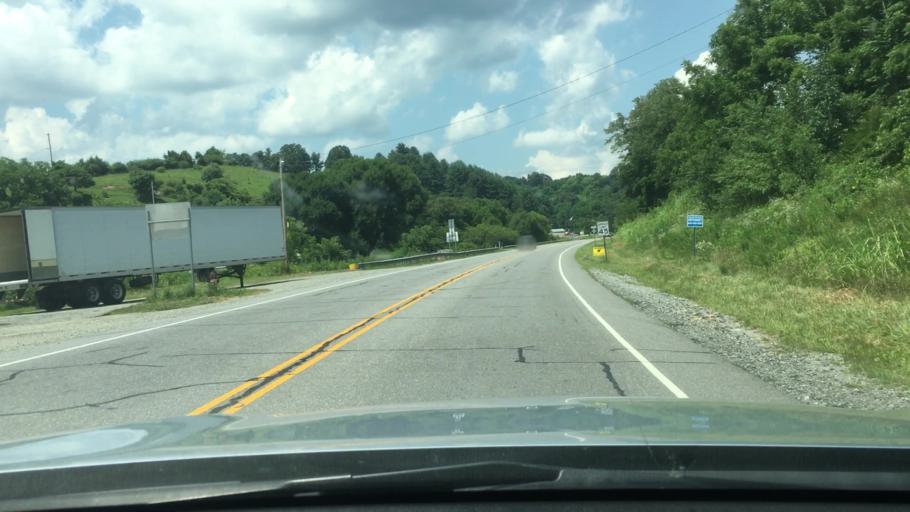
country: US
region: North Carolina
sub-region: Madison County
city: Marshall
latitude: 35.8051
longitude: -82.6583
